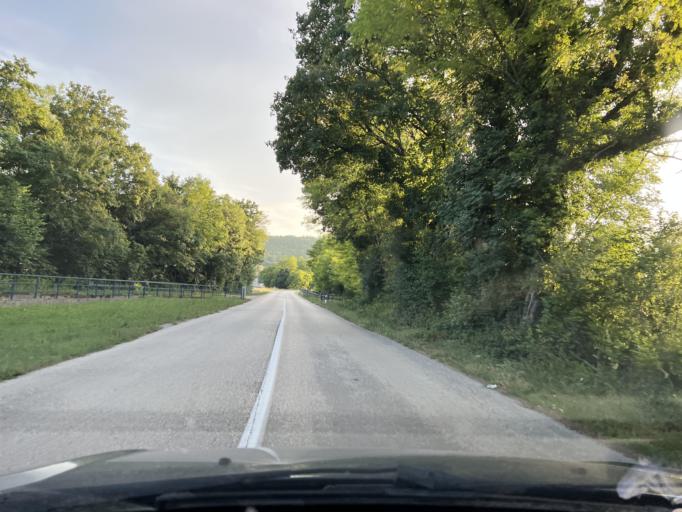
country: HR
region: Primorsko-Goranska
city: Podhum
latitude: 45.3758
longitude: 14.4807
